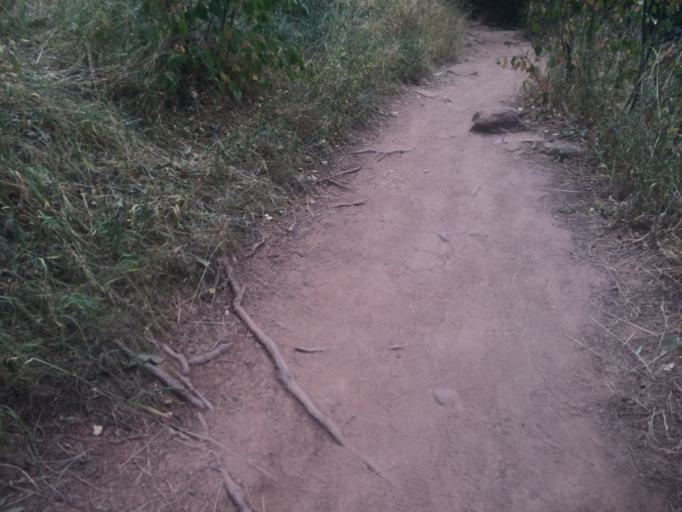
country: US
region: Colorado
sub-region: Boulder County
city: Boulder
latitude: 39.9762
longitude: -105.2837
